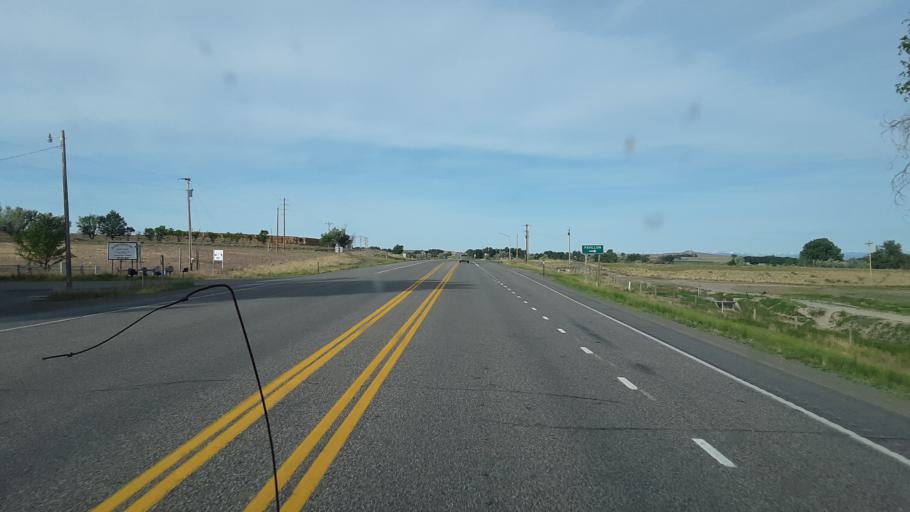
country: US
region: Wyoming
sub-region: Fremont County
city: Riverton
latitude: 43.1873
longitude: -108.2442
